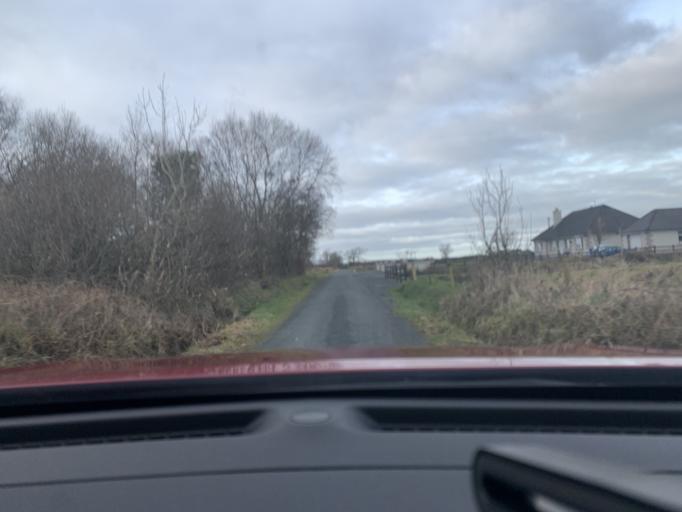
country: IE
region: Connaught
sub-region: Roscommon
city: Ballaghaderreen
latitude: 53.9788
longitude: -8.5577
